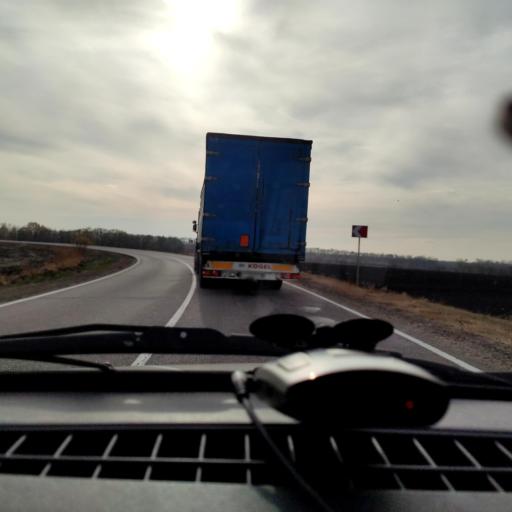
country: RU
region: Voronezj
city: Strelitsa
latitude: 51.4688
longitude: 38.9593
